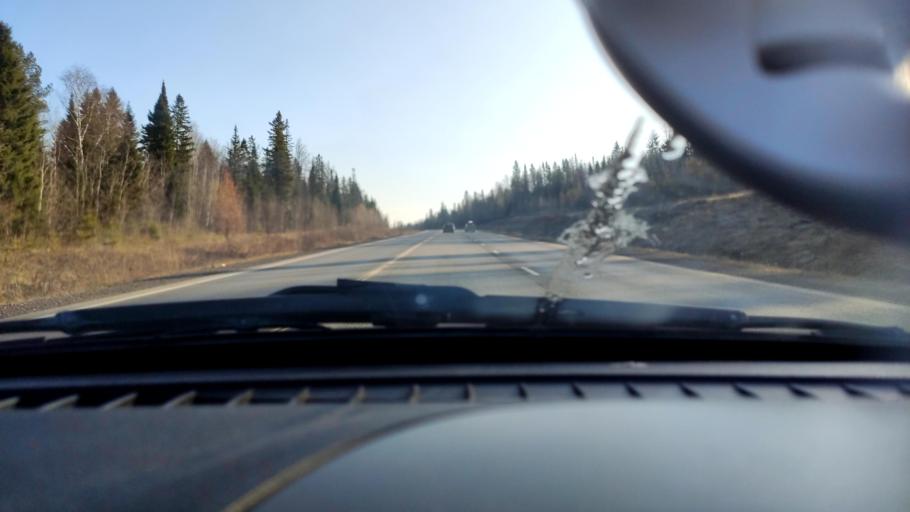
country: RU
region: Perm
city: Novyye Lyady
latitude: 58.0350
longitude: 56.4749
